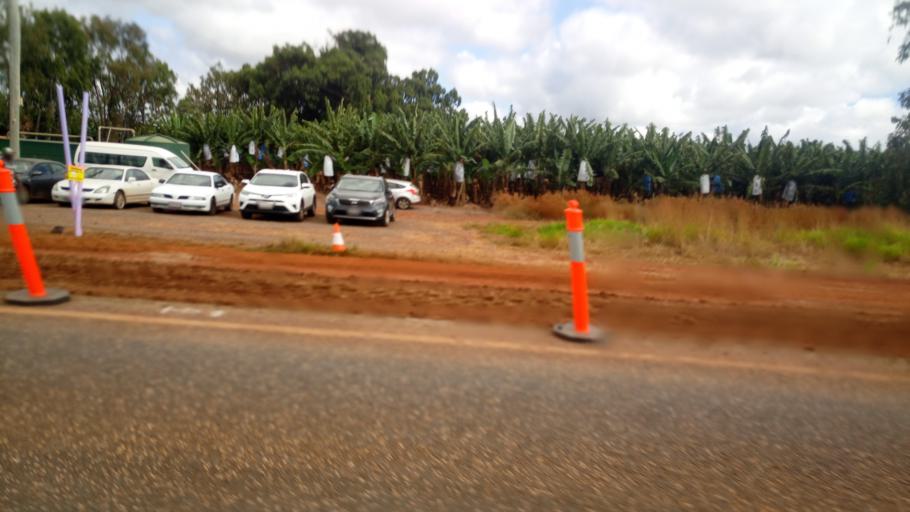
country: AU
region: Queensland
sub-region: Tablelands
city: Mareeba
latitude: -17.0847
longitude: 145.4351
